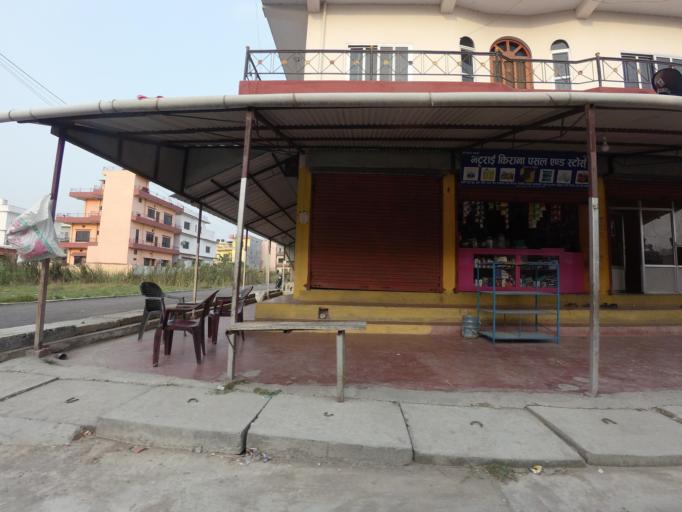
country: NP
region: Western Region
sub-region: Lumbini Zone
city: Bhairahawa
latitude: 27.5125
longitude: 83.4591
